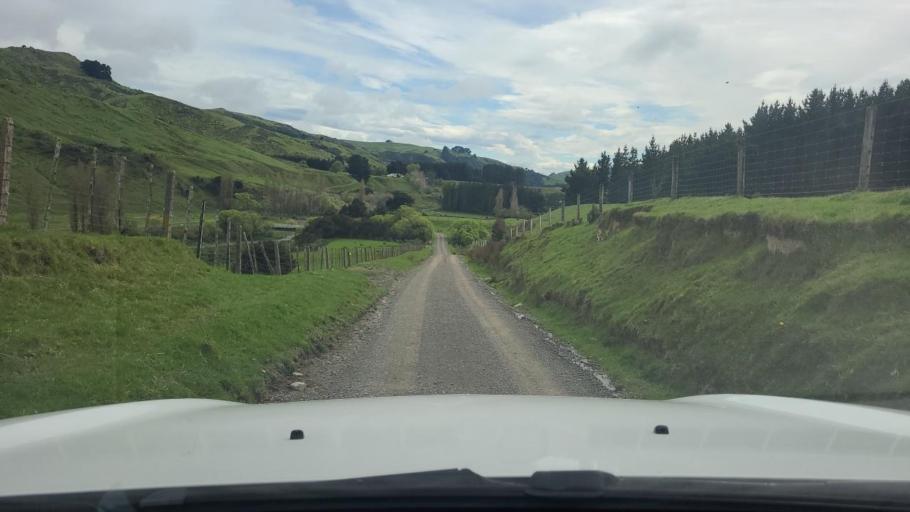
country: NZ
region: Wellington
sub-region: South Wairarapa District
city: Waipawa
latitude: -41.3894
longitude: 175.4524
